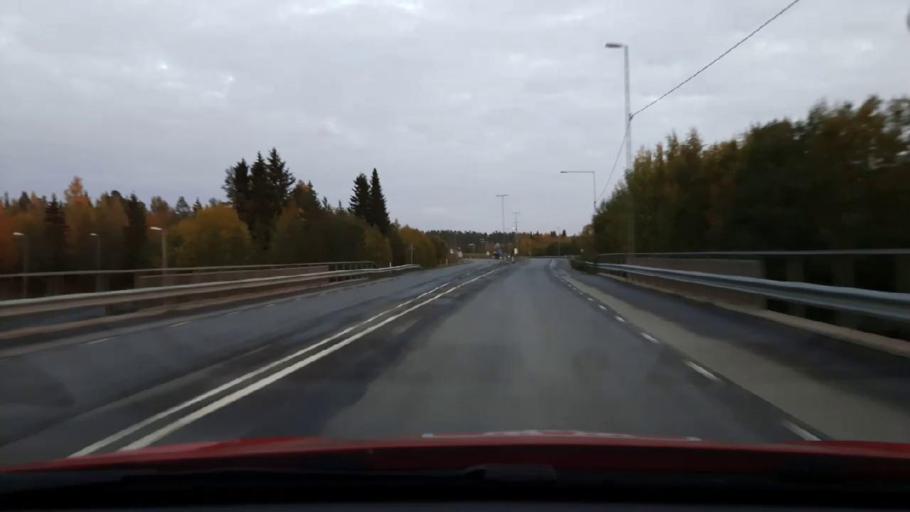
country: SE
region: Jaemtland
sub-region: OEstersunds Kommun
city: Ostersund
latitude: 63.2013
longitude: 14.6423
